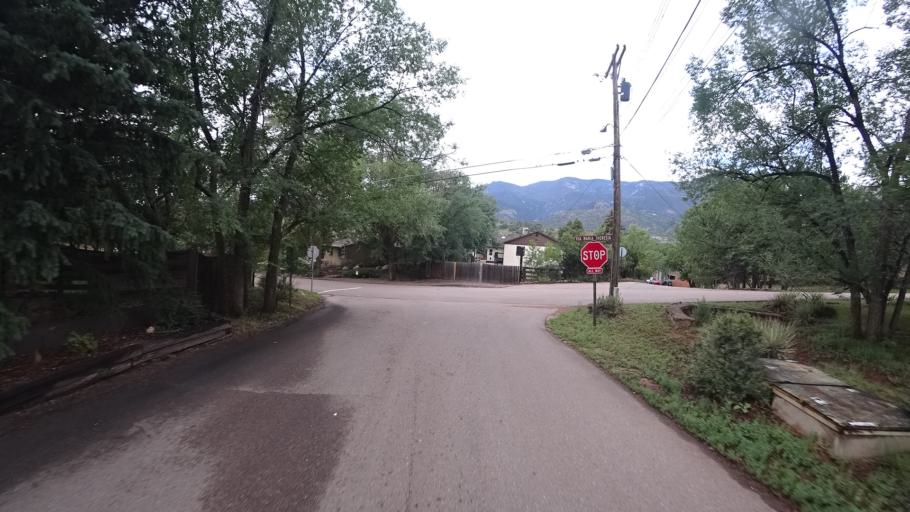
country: US
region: Colorado
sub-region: El Paso County
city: Manitou Springs
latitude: 38.8603
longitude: -104.8886
